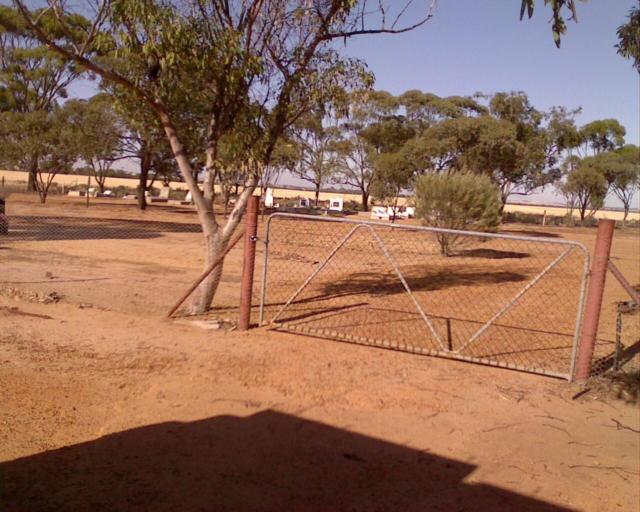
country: AU
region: Western Australia
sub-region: Merredin
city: Merredin
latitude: -31.1104
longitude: 117.7864
